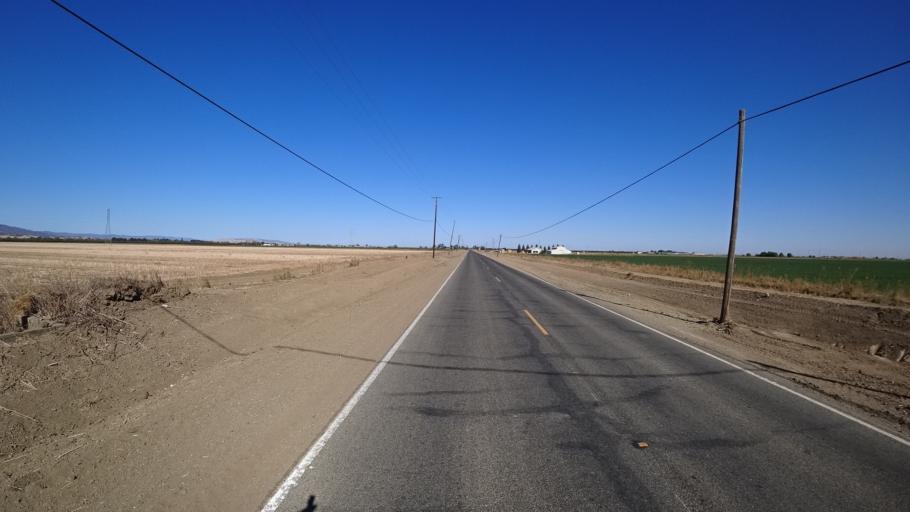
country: US
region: California
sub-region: Yolo County
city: Cottonwood
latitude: 38.6096
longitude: -121.9715
